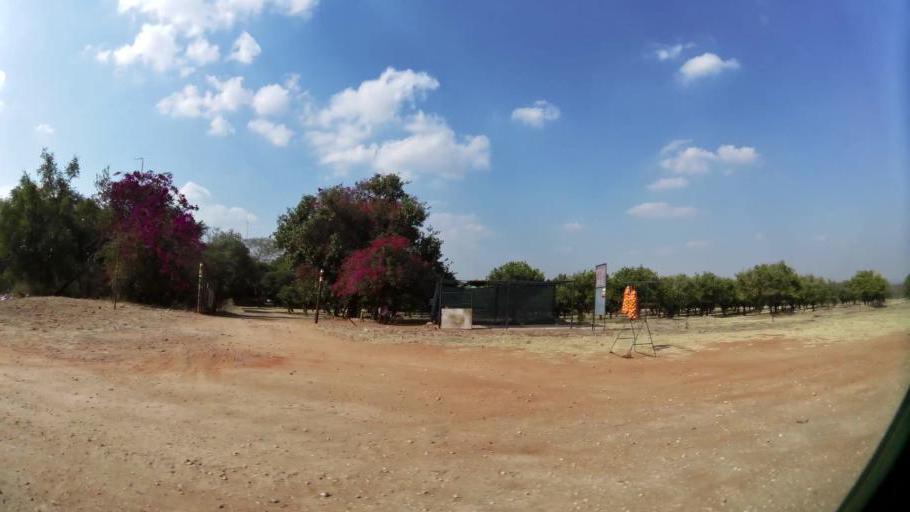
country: ZA
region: North-West
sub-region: Bojanala Platinum District Municipality
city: Mogwase
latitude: -25.4720
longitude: 27.0871
